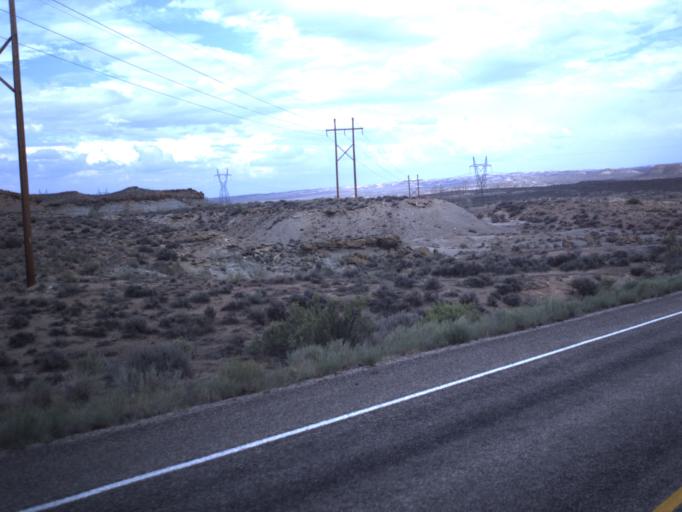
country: US
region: Colorado
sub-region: Rio Blanco County
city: Rangely
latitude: 40.0743
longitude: -109.2067
